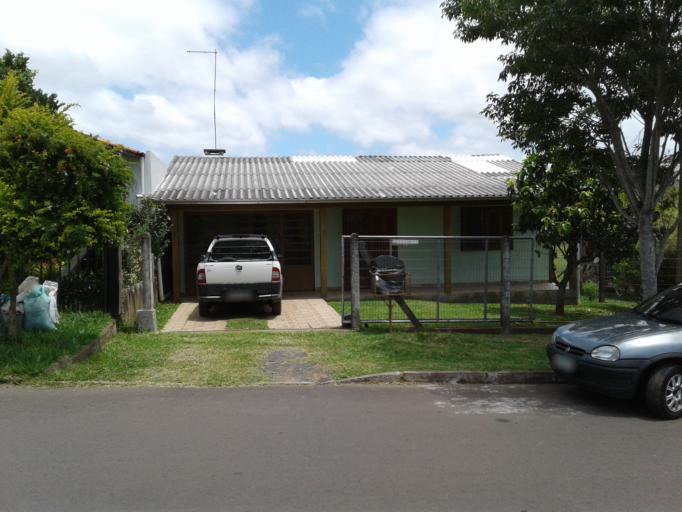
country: BR
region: Rio Grande do Sul
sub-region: Gravatai
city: Gravatai
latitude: -29.8789
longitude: -50.7812
